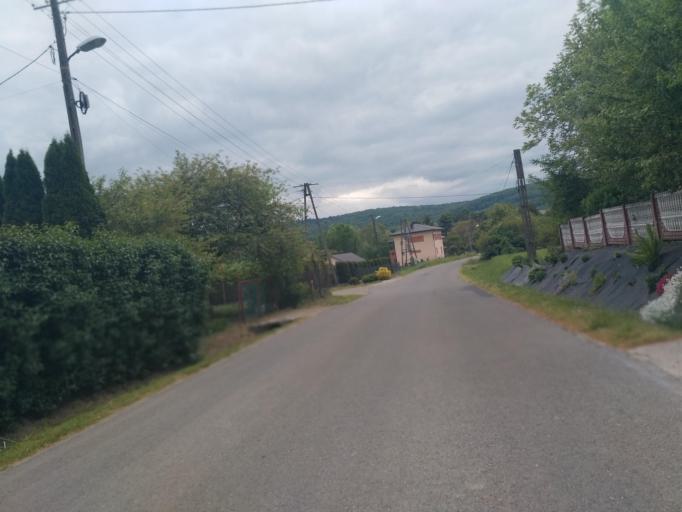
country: PL
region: Subcarpathian Voivodeship
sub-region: Powiat krosnienski
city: Jedlicze
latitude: 49.6970
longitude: 21.6397
